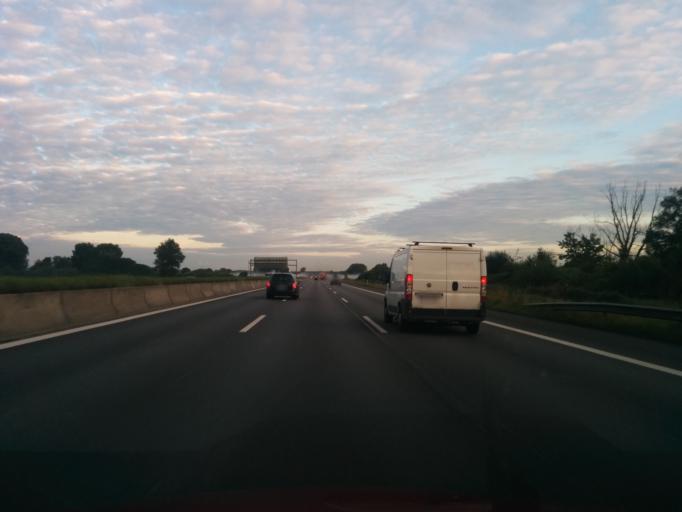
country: DE
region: Bavaria
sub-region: Upper Bavaria
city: Bergkirchen
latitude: 48.2406
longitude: 11.3352
